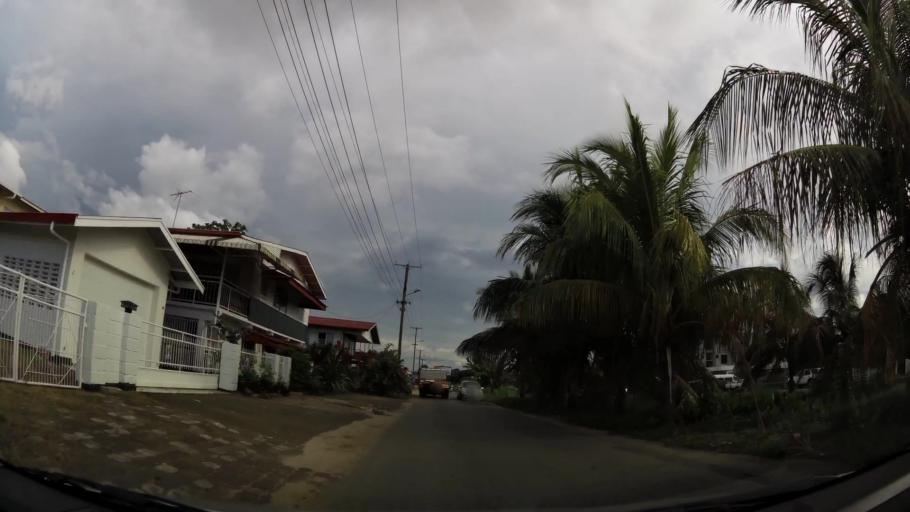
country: SR
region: Paramaribo
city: Paramaribo
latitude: 5.8494
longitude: -55.1835
